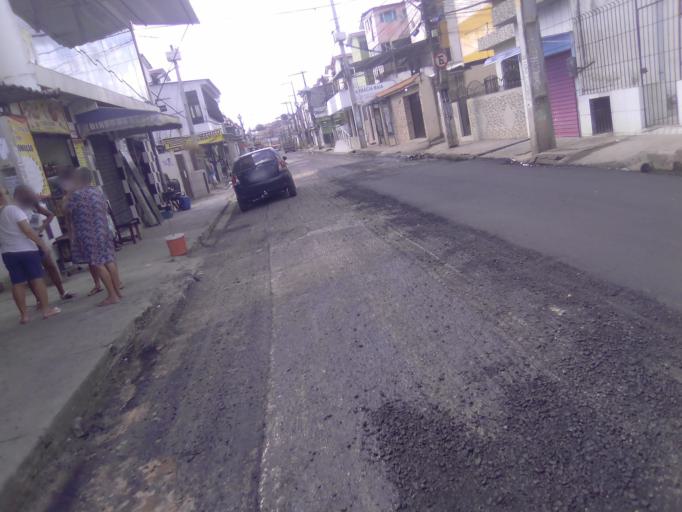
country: BR
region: Pernambuco
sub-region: Jaboatao Dos Guararapes
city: Jaboatao dos Guararapes
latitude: -8.0701
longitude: -34.9955
